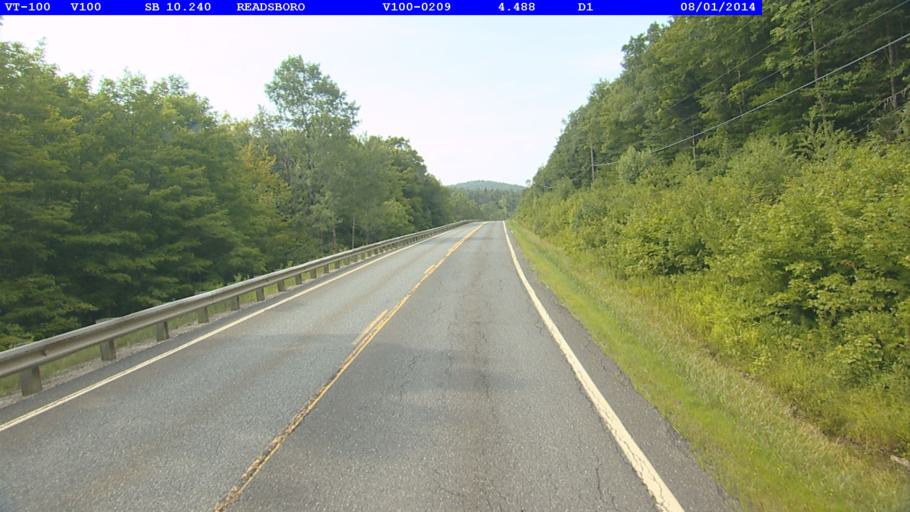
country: US
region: Massachusetts
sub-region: Berkshire County
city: North Adams
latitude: 42.8001
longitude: -72.9718
